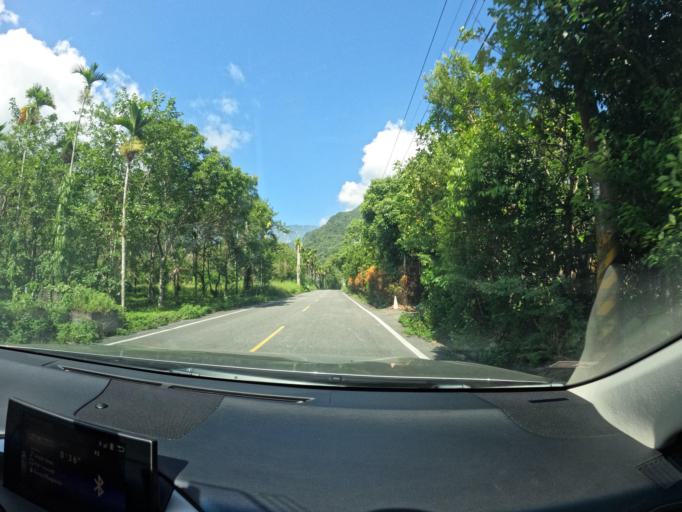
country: TW
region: Taiwan
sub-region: Hualien
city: Hualian
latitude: 23.5867
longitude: 121.3587
